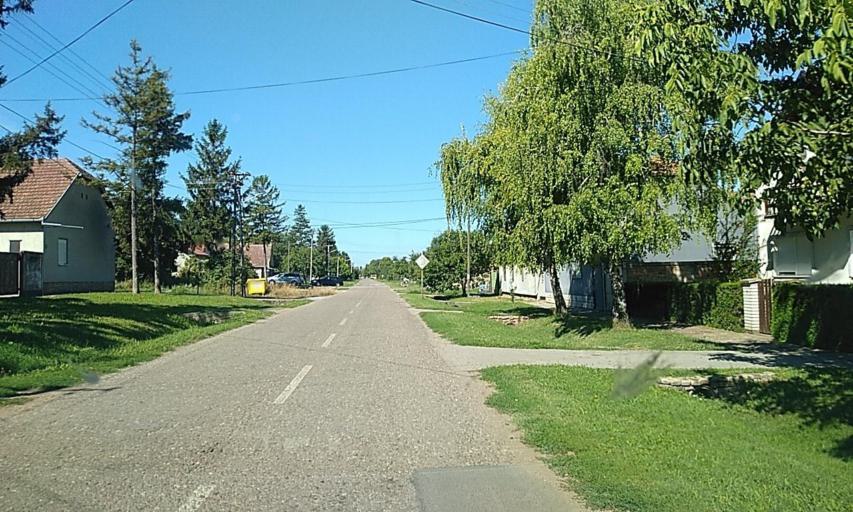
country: RS
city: Backo Gradiste
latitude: 45.5356
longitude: 20.0304
